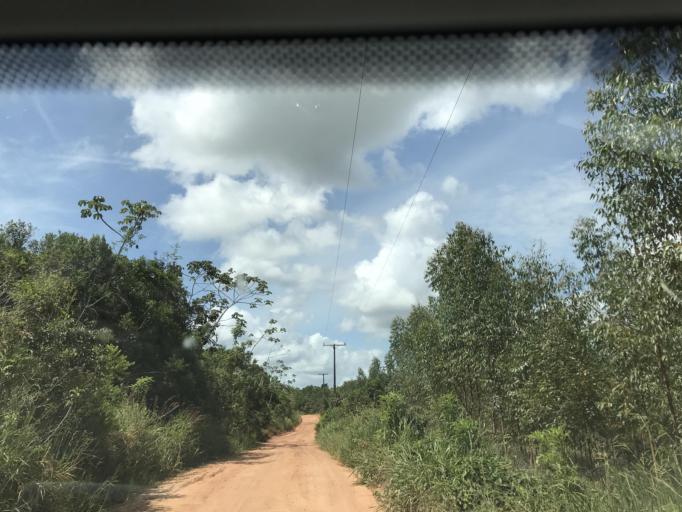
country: BR
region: Bahia
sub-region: Entre Rios
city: Entre Rios
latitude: -12.2201
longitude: -38.0840
